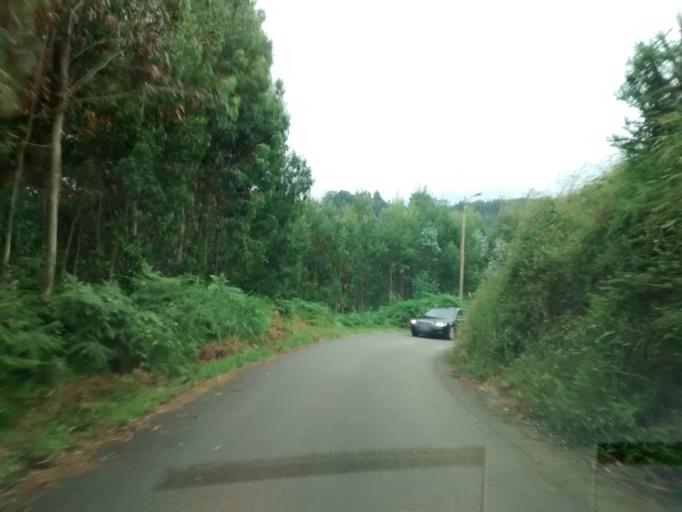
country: ES
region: Asturias
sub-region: Province of Asturias
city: Villaviciosa
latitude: 43.5426
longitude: -5.4081
